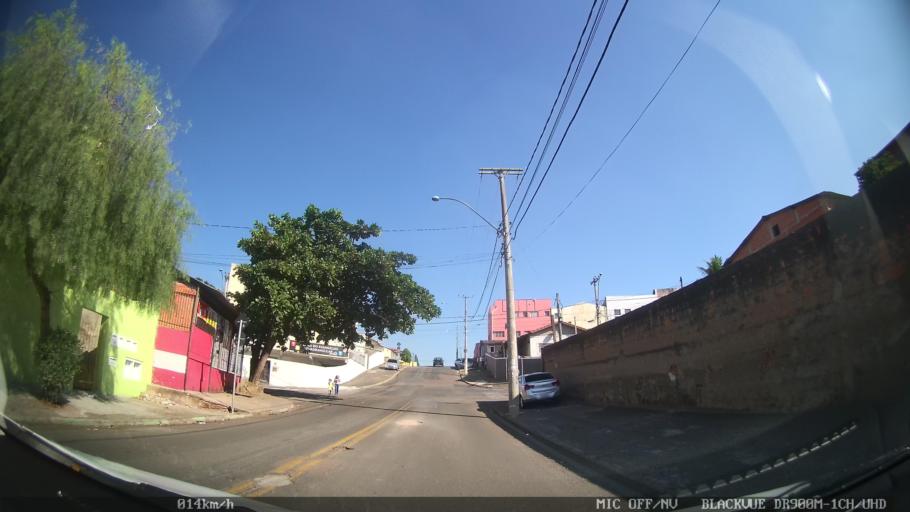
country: BR
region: Sao Paulo
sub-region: Campinas
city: Campinas
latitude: -22.9584
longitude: -47.0929
